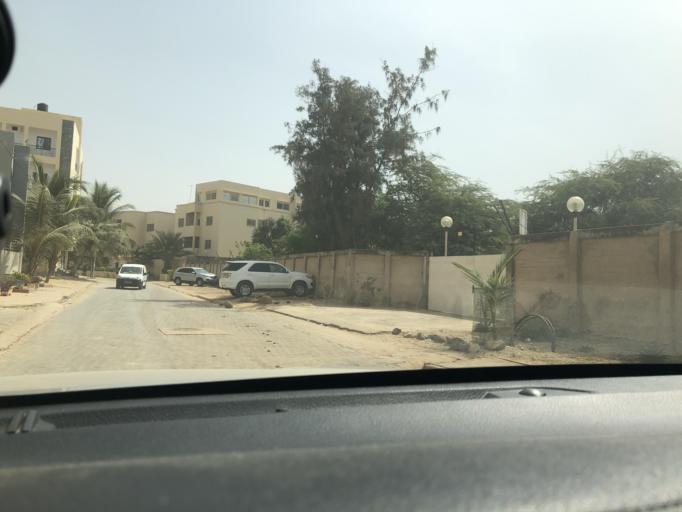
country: SN
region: Dakar
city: Mermoz Boabab
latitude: 14.7449
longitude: -17.5163
